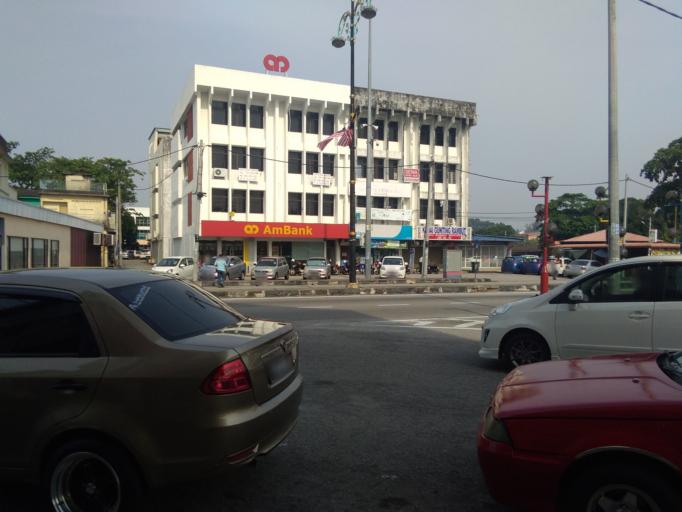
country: MY
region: Kedah
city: Kulim
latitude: 5.3721
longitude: 100.5555
